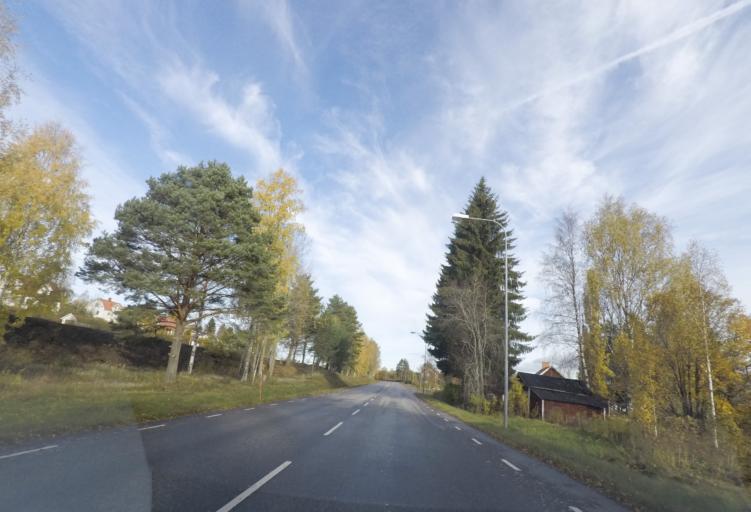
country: SE
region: OErebro
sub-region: Ljusnarsbergs Kommun
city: Kopparberg
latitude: 59.9300
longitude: 14.9456
